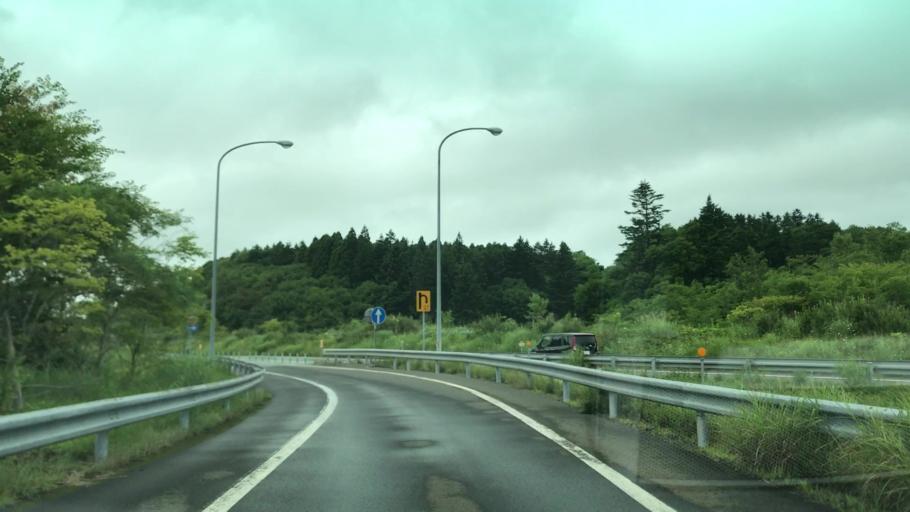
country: JP
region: Hokkaido
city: Muroran
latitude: 42.3846
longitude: 140.9876
